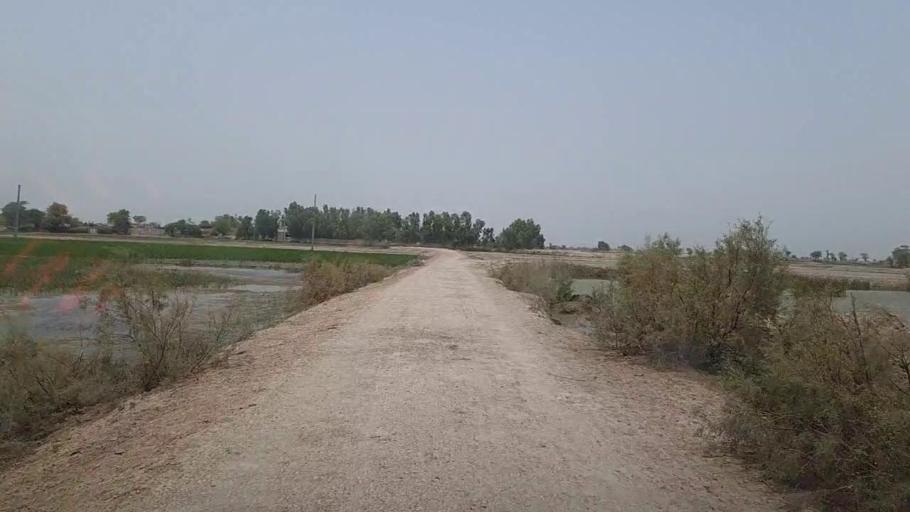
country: PK
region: Sindh
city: Sita Road
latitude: 27.0691
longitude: 67.8464
